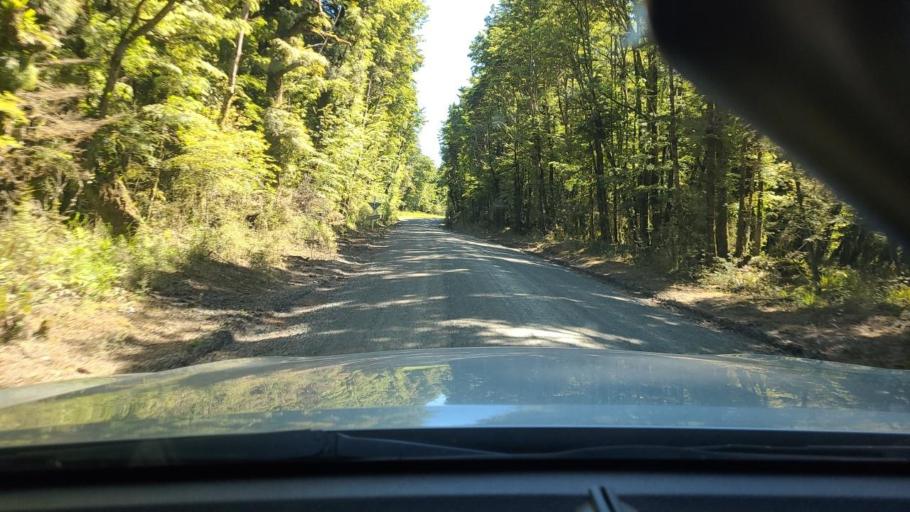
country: NZ
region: Southland
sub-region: Southland District
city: Riverton
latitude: -45.9587
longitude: 167.6725
